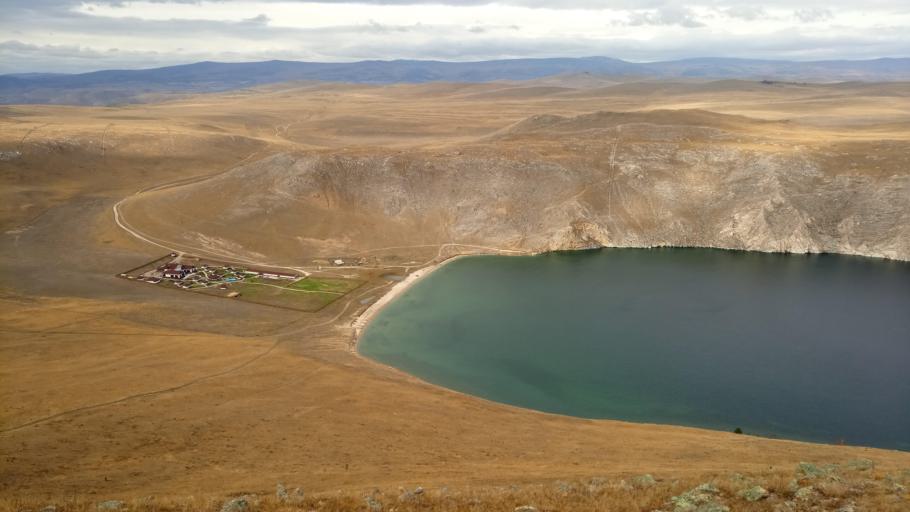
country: RU
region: Irkutsk
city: Yelantsy
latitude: 52.7824
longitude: 106.6121
